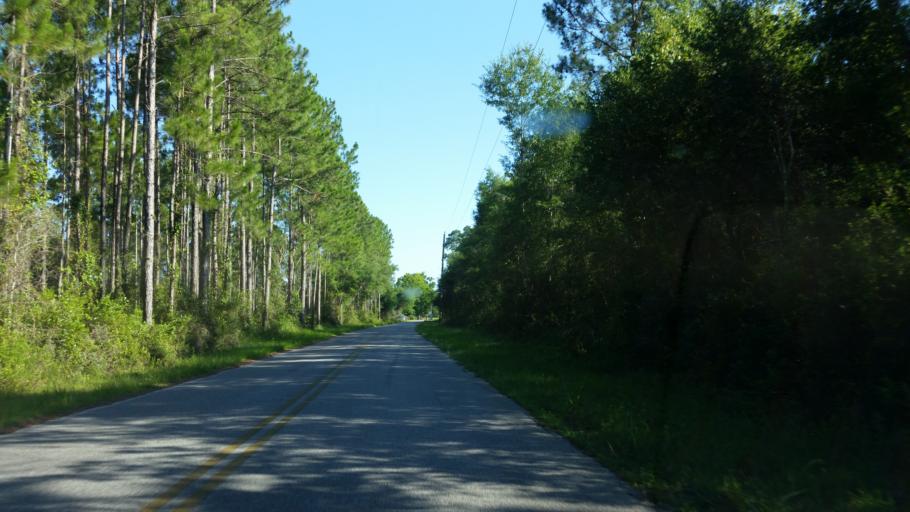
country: US
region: Florida
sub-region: Escambia County
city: Bellview
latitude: 30.4648
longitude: -87.4095
